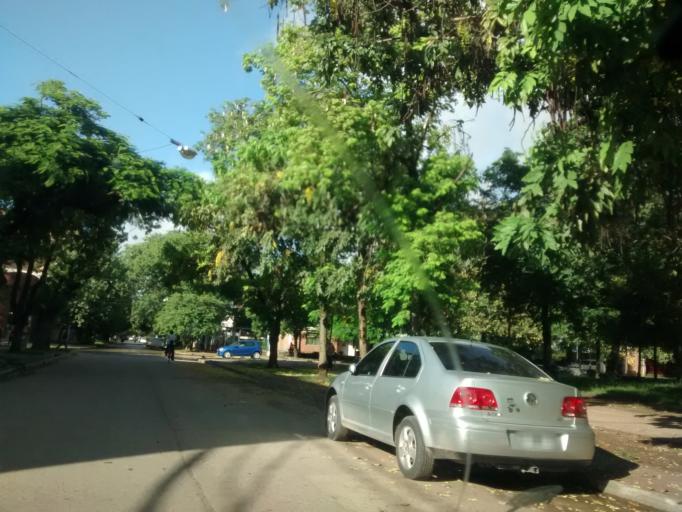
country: AR
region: Chaco
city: Resistencia
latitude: -27.4507
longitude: -58.9792
